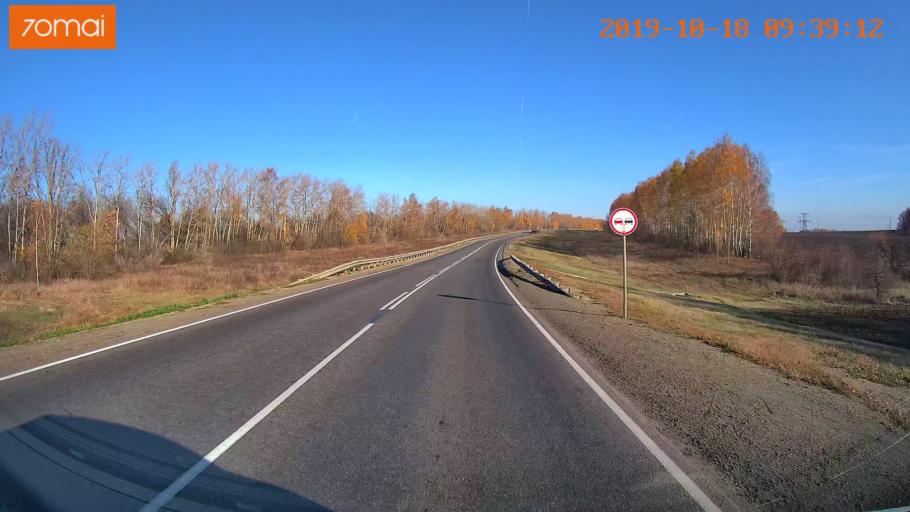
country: RU
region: Tula
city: Yefremov
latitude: 53.2497
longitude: 38.1342
